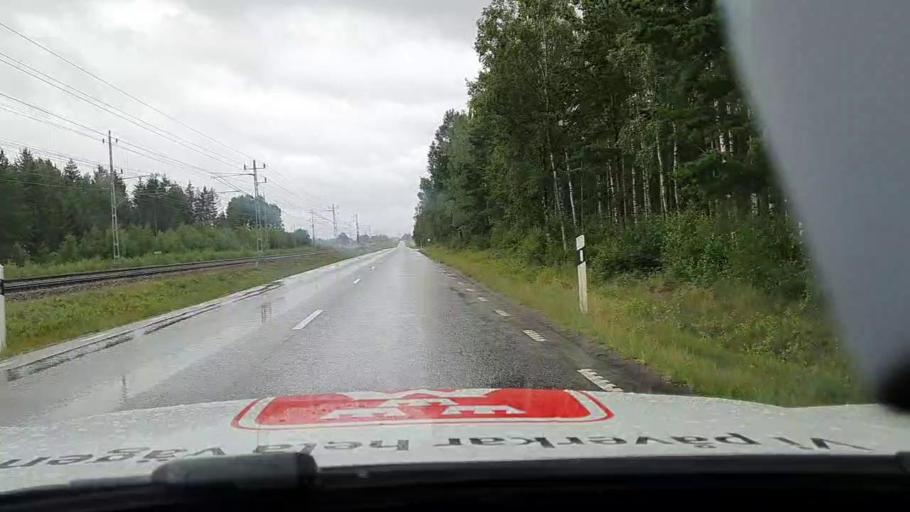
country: SE
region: Vaestra Goetaland
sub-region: Toreboda Kommun
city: Toereboda
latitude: 58.6607
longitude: 14.0874
